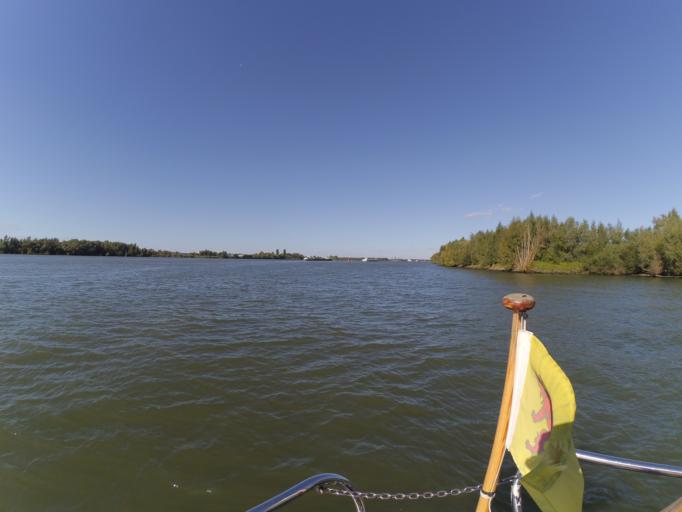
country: NL
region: South Holland
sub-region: Gemeente Binnenmaas
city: Heinenoord
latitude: 51.8332
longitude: 4.4514
